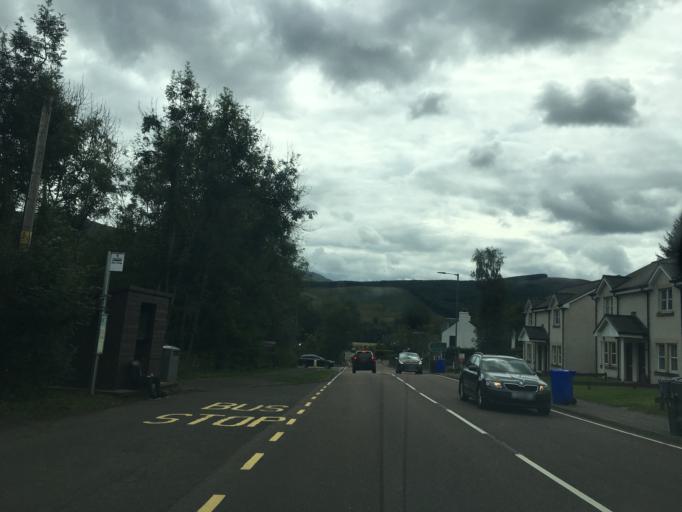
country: GB
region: Scotland
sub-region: Stirling
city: Callander
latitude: 56.3862
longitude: -4.2878
